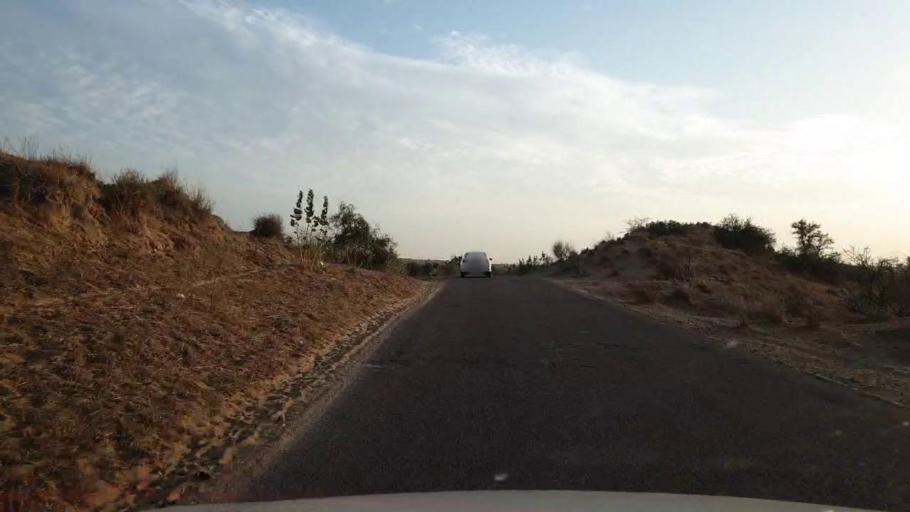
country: PK
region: Sindh
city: Nabisar
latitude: 25.0170
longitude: 69.9391
